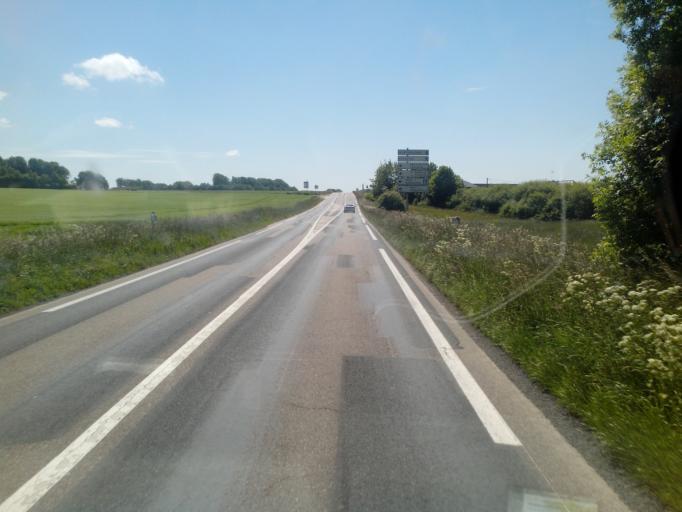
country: FR
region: Haute-Normandie
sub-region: Departement de la Seine-Maritime
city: Turretot
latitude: 49.6060
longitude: 0.2815
